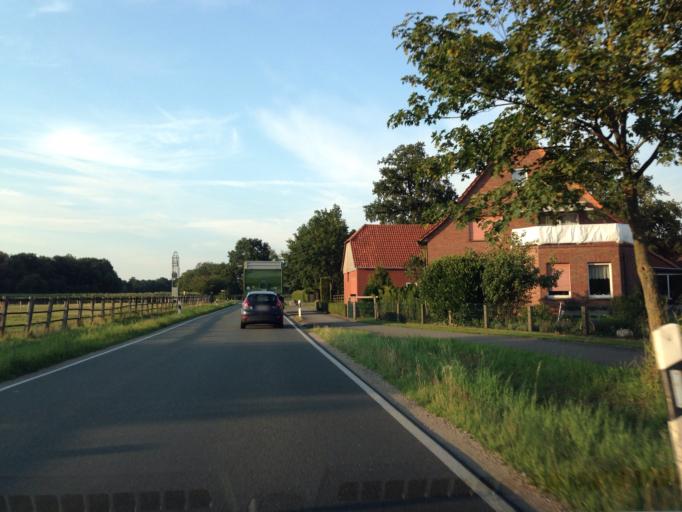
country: DE
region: North Rhine-Westphalia
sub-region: Regierungsbezirk Munster
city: Senden
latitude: 51.8310
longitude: 7.5404
